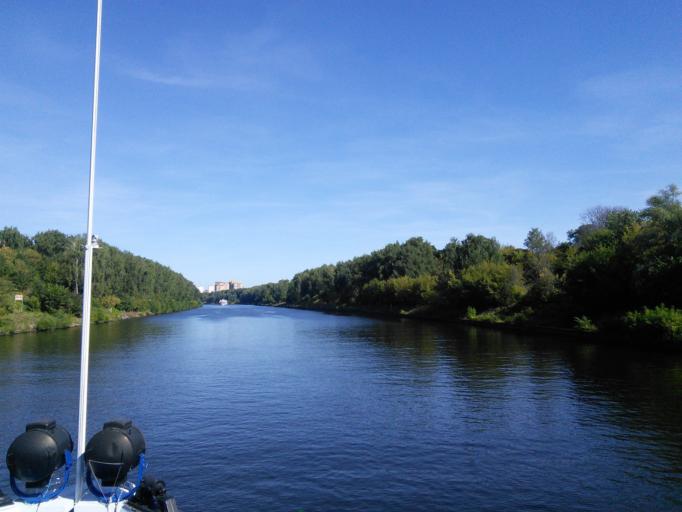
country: RU
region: Moskovskaya
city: Dolgoprudnyy
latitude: 55.9185
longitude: 37.4880
